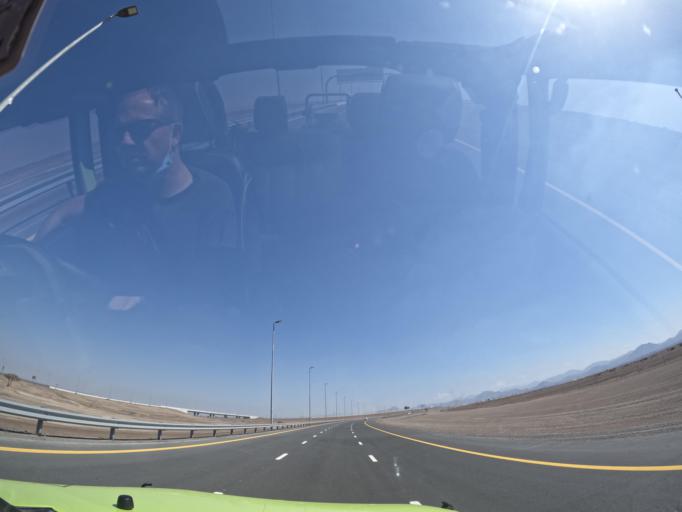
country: AE
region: Ash Shariqah
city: Adh Dhayd
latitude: 25.1156
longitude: 55.9397
